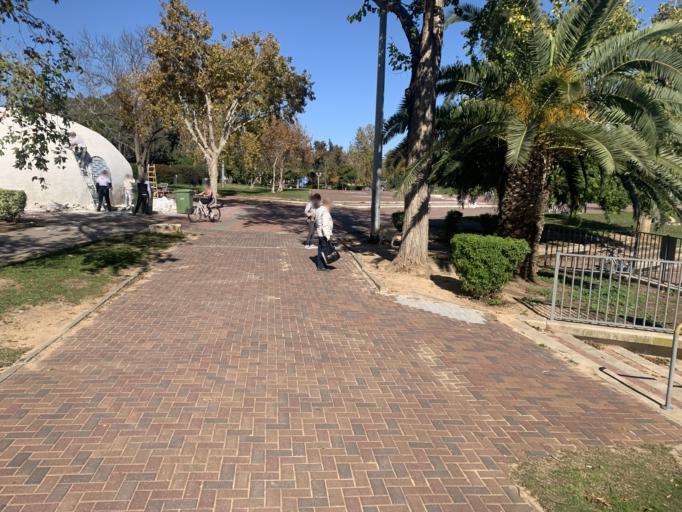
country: IL
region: Tel Aviv
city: Ramat Gan
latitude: 32.0980
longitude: 34.8091
